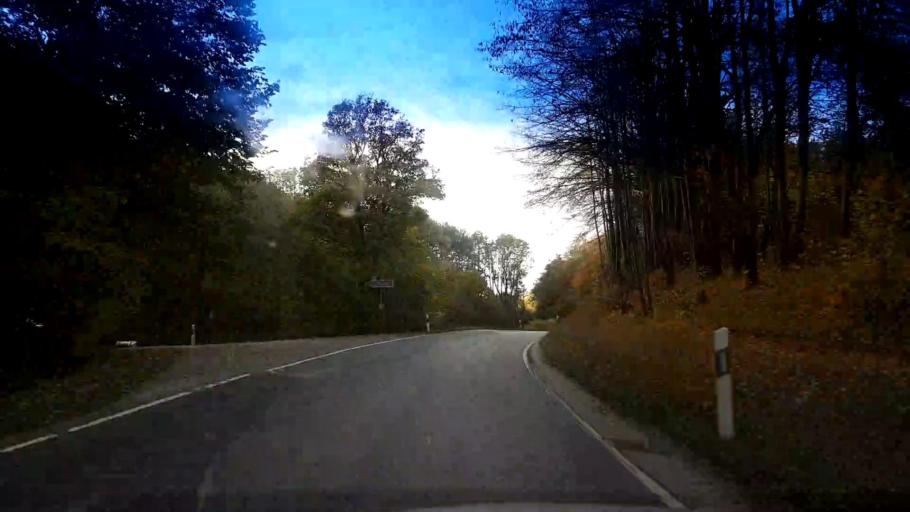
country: DE
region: Bavaria
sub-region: Upper Franconia
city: Poxdorf
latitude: 49.9509
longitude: 11.0780
